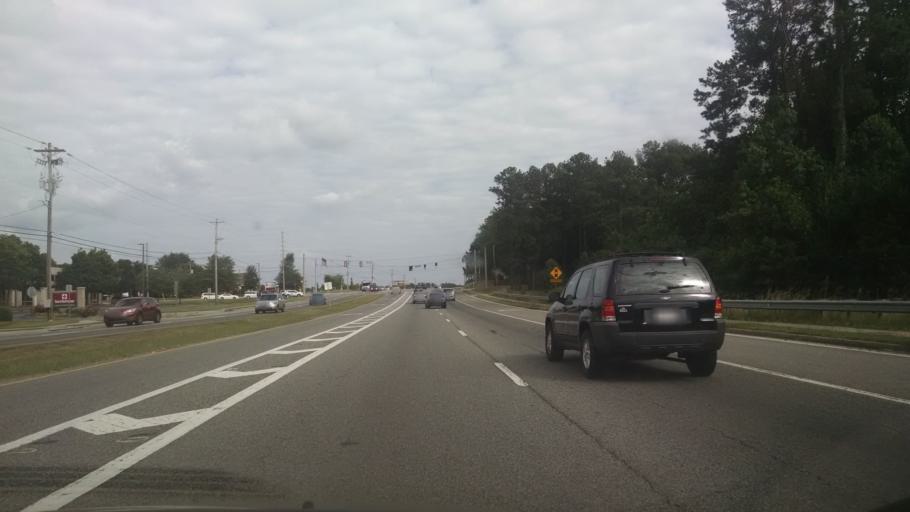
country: US
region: Georgia
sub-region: Forsyth County
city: Cumming
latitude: 34.1783
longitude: -84.1318
